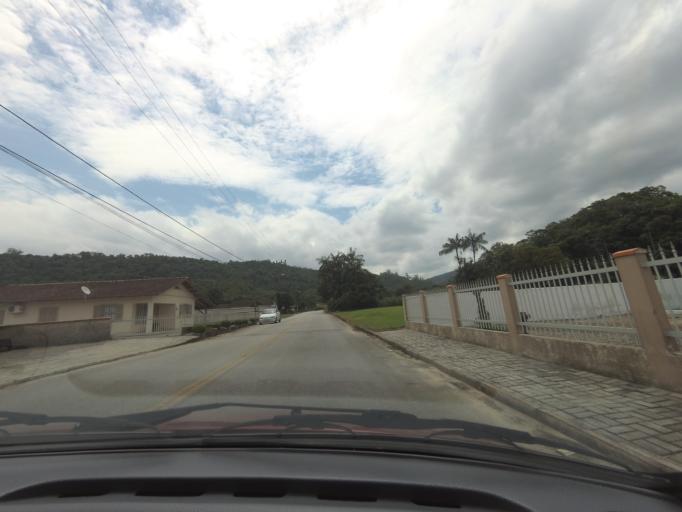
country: BR
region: Santa Catarina
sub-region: Brusque
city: Brusque
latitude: -27.0653
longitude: -48.9856
